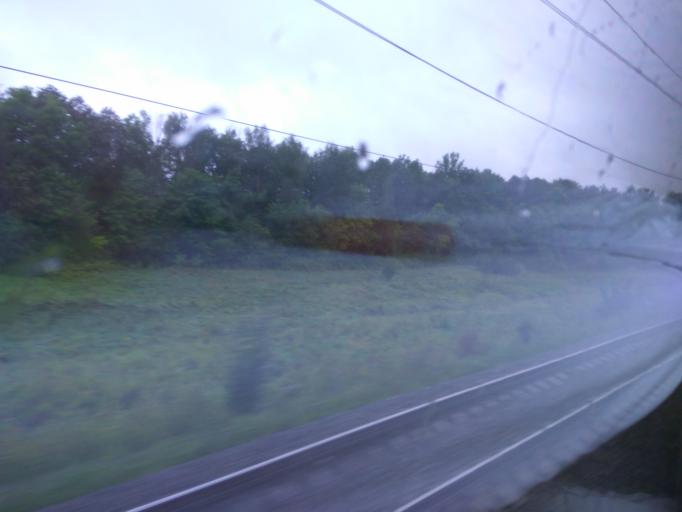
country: RU
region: Moskovskaya
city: Kashira
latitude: 54.8523
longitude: 38.2183
